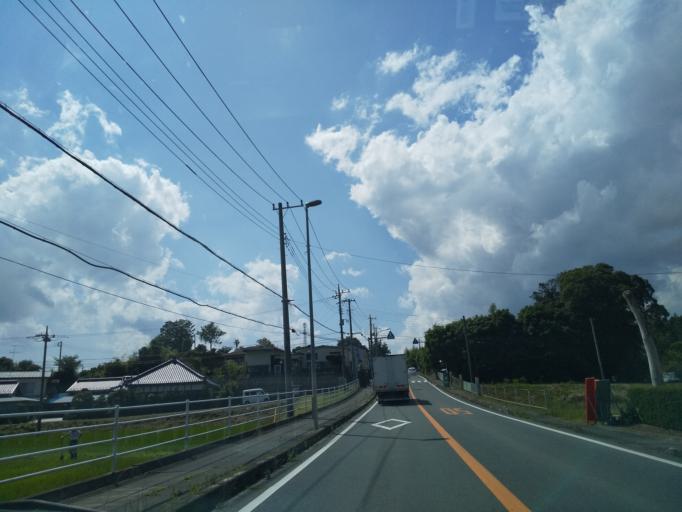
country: JP
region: Ibaraki
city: Ishioka
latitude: 36.1637
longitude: 140.3696
